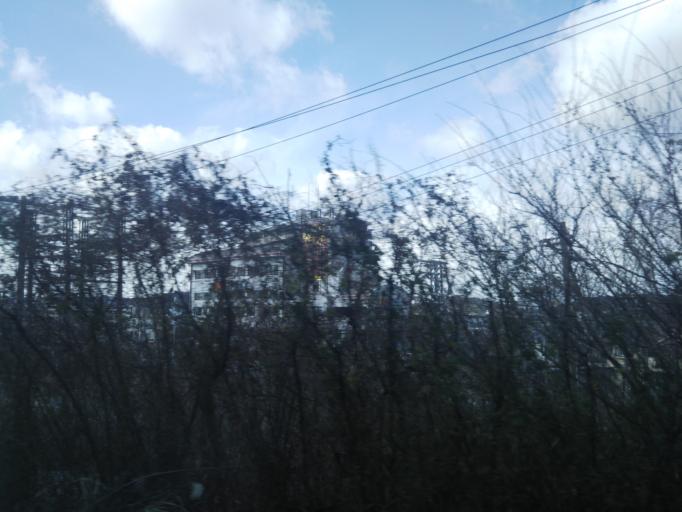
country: JP
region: Okayama
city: Okayama-shi
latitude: 34.6607
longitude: 133.9105
